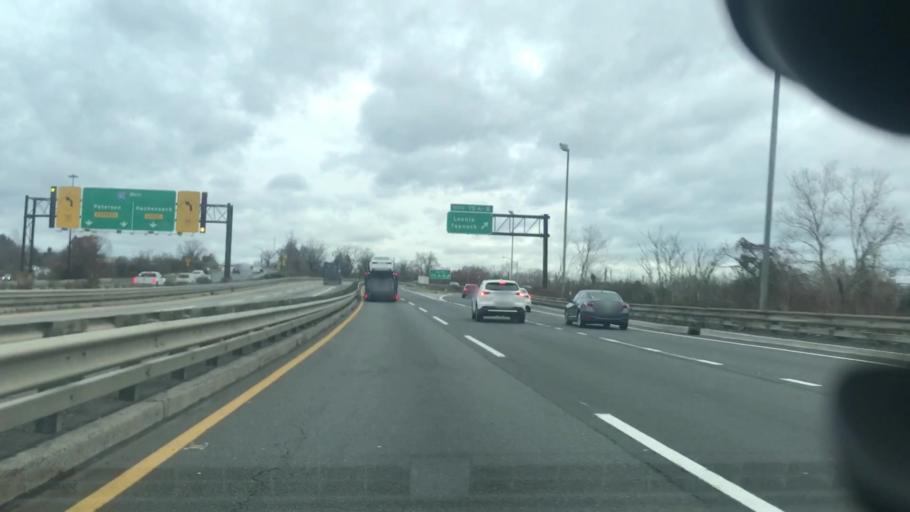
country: US
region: New Jersey
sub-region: Bergen County
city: Ridgefield Park
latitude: 40.8609
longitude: -74.0112
